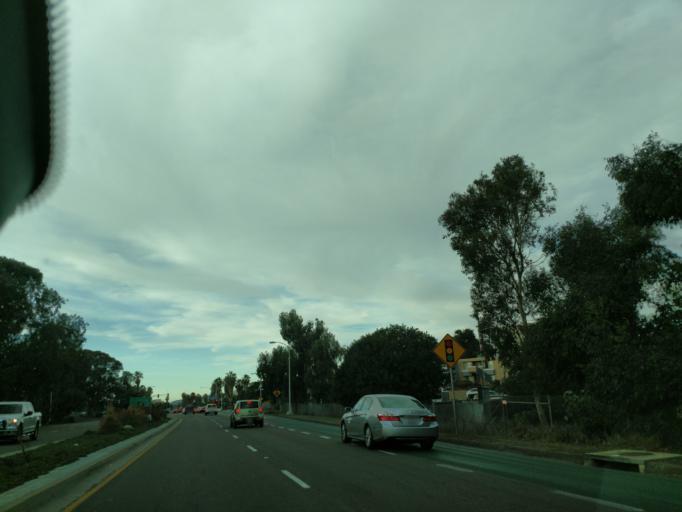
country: US
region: California
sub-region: San Diego County
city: Coronado
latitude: 32.7493
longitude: -117.2351
